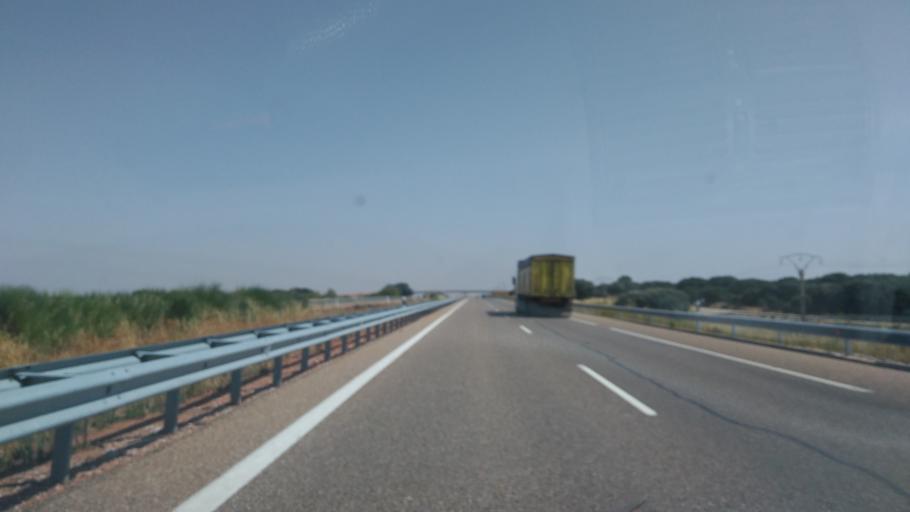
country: ES
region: Castille and Leon
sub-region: Provincia de Salamanca
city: Galindo y Perahuy
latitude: 40.9232
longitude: -5.8395
